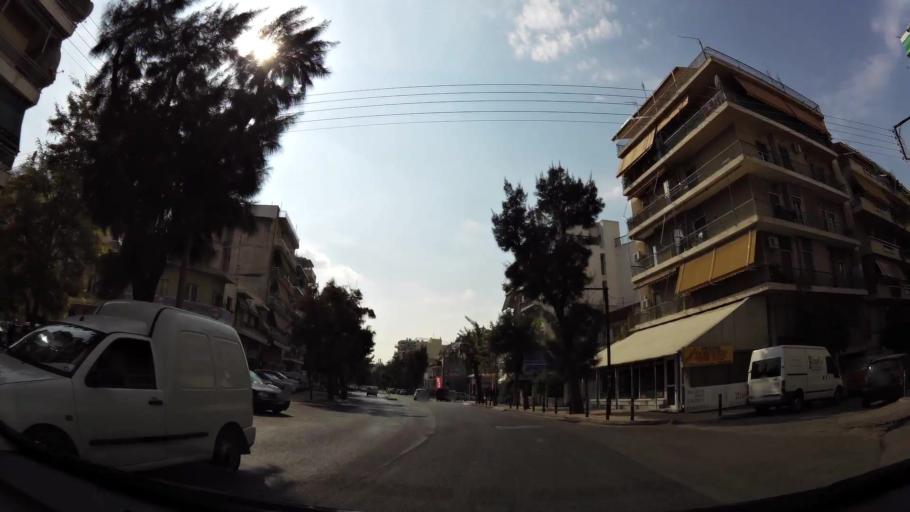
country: GR
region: Attica
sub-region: Nomarchia Athinas
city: Nea Chalkidona
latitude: 38.0227
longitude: 23.7393
